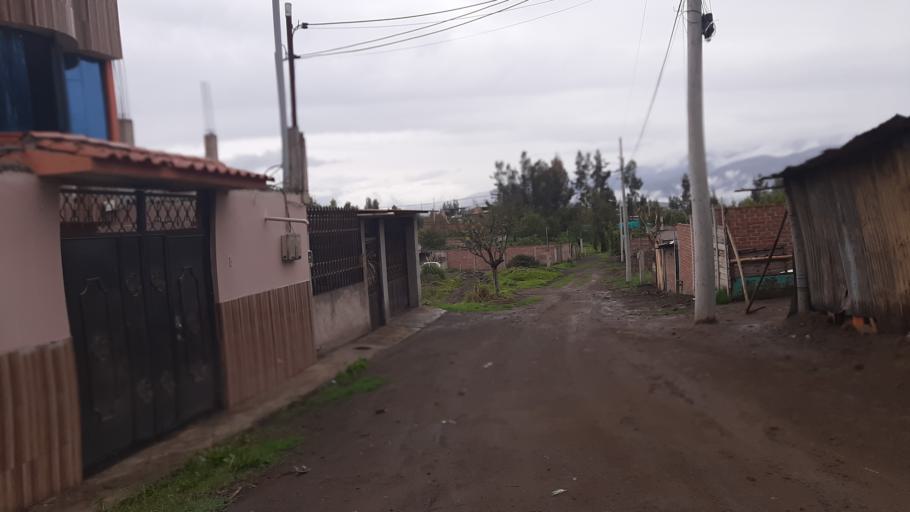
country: EC
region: Chimborazo
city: Riobamba
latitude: -1.6524
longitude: -78.6372
